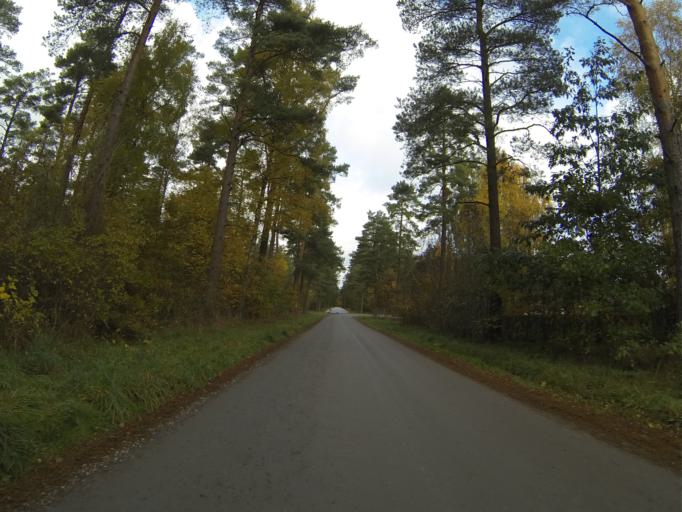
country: SE
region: Skane
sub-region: Sjobo Kommun
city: Sjoebo
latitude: 55.6331
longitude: 13.6432
